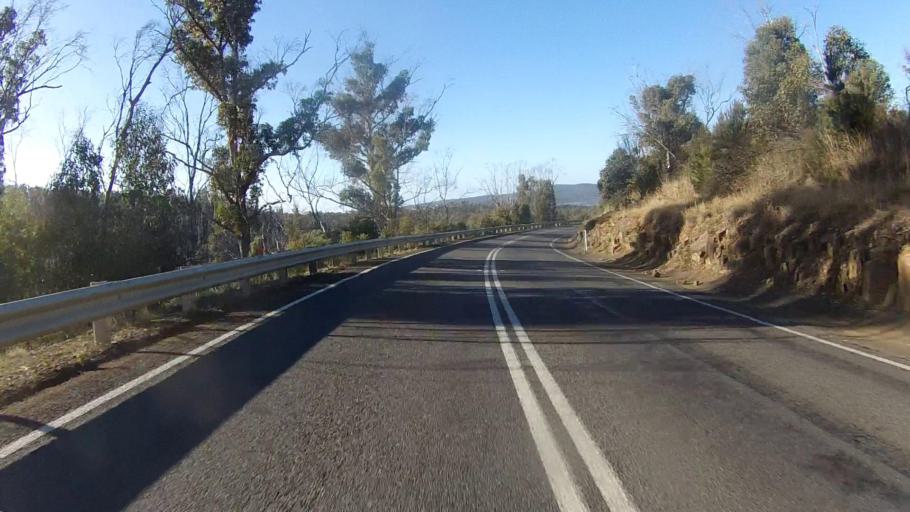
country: AU
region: Tasmania
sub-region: Sorell
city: Sorell
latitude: -42.8450
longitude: 147.8127
